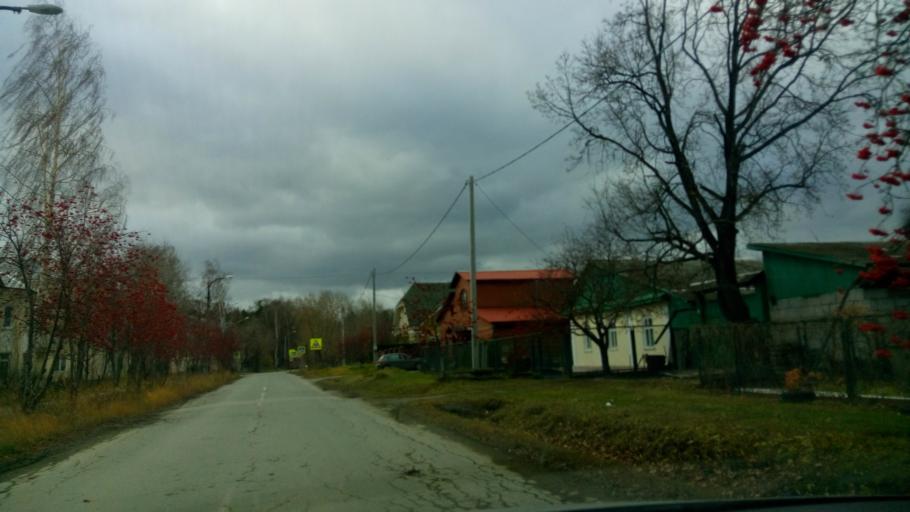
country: RU
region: Sverdlovsk
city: Sredneuralsk
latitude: 56.9910
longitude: 60.4725
